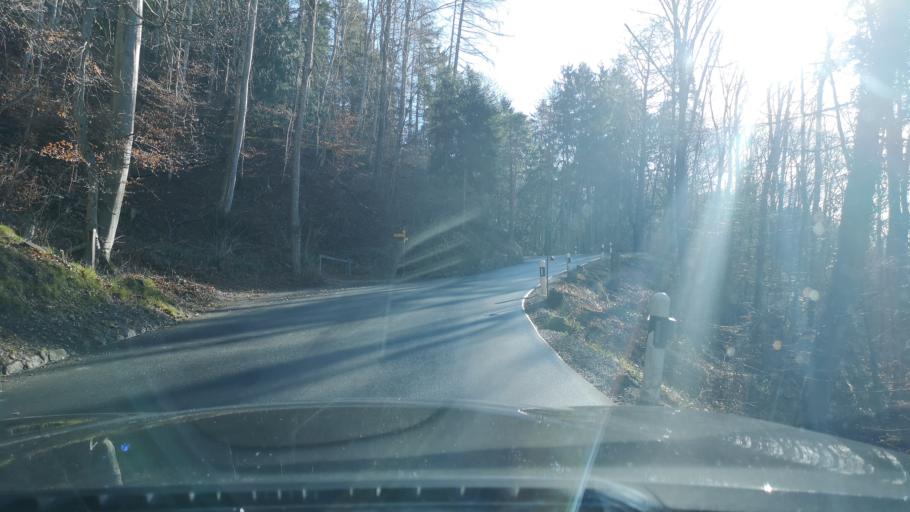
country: LI
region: Vaduz
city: Vaduz
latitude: 47.1365
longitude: 9.5273
